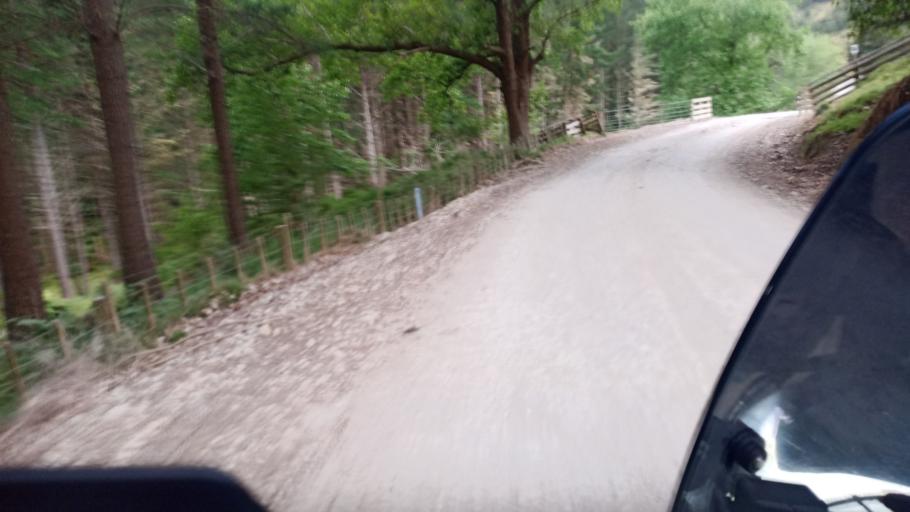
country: NZ
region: Gisborne
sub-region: Gisborne District
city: Gisborne
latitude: -38.4809
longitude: 177.9635
